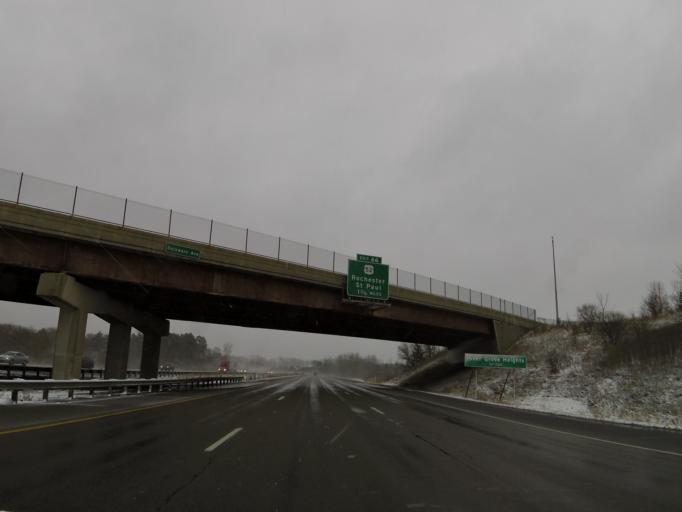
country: US
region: Minnesota
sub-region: Dakota County
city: Mendota Heights
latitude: 44.8611
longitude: -93.1065
